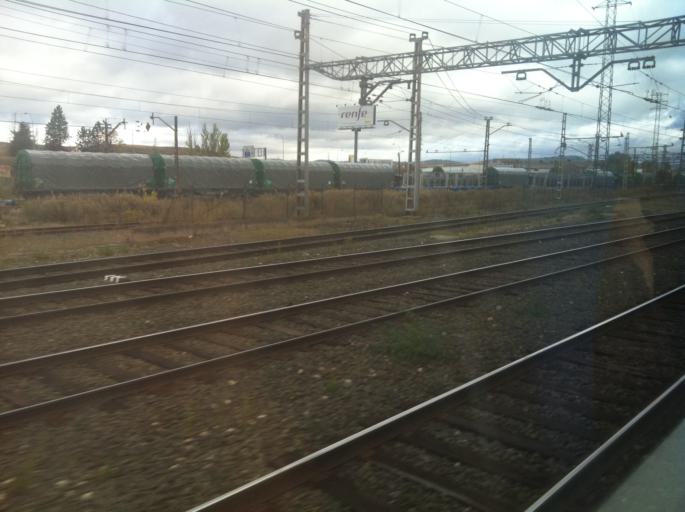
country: ES
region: Castille and Leon
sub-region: Provincia de Burgos
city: Miranda de Ebro
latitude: 42.6889
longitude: -2.9481
